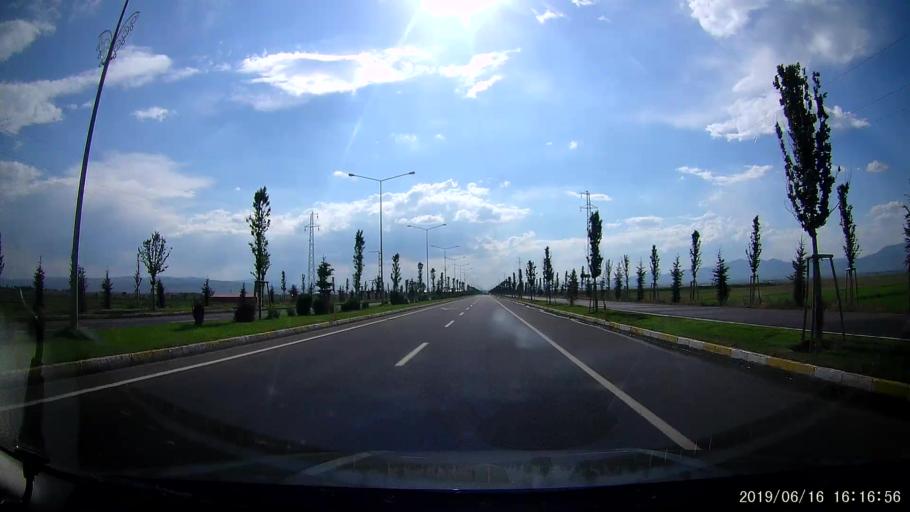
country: TR
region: Erzurum
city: Ilica
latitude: 39.9634
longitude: 41.1980
